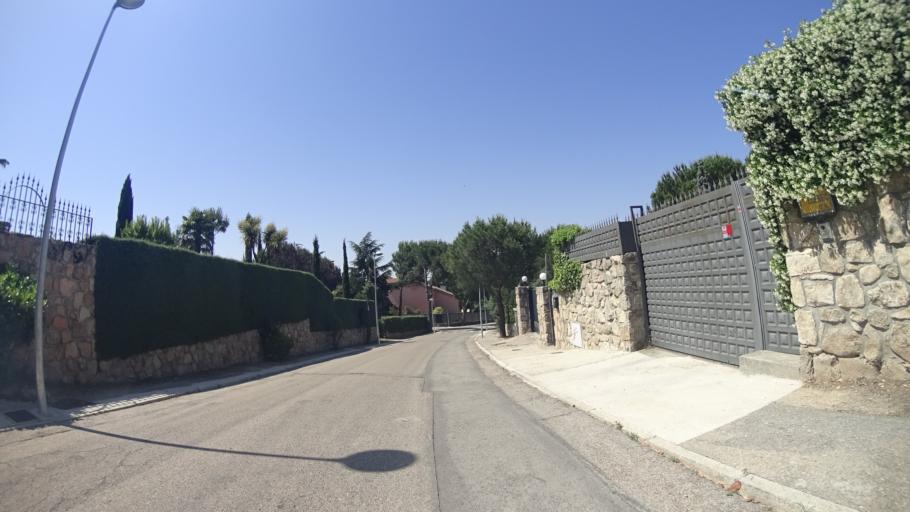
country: ES
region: Madrid
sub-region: Provincia de Madrid
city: Torrelodones
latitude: 40.5829
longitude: -3.9213
